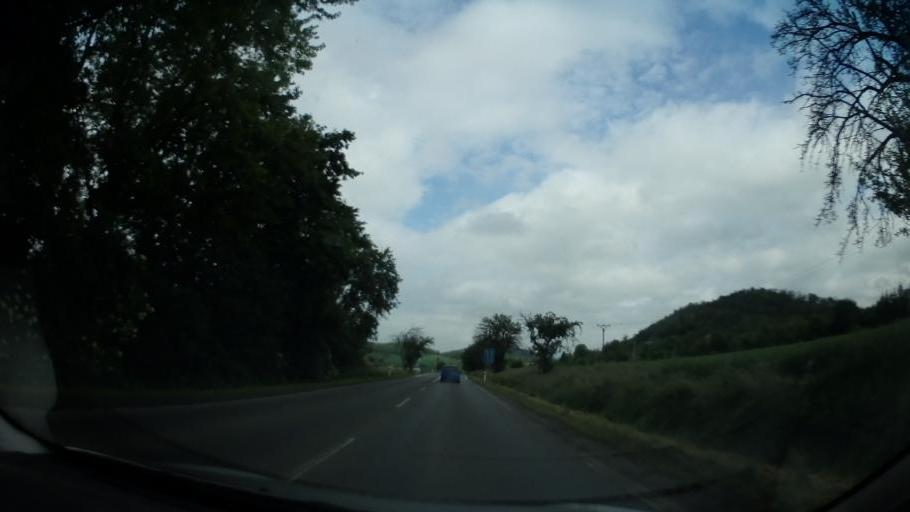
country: CZ
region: South Moravian
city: Kurim
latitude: 49.2996
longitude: 16.5193
